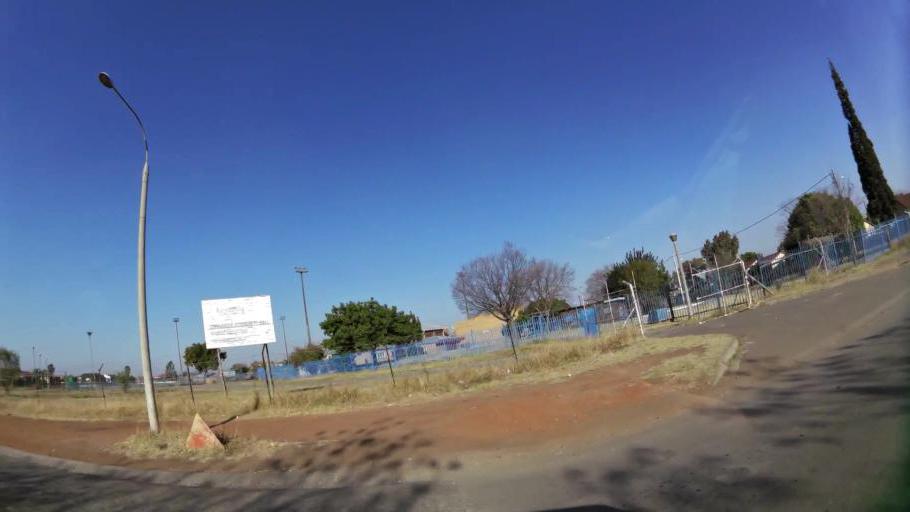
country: ZA
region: North-West
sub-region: Bojanala Platinum District Municipality
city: Rustenburg
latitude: -25.6462
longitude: 27.2420
